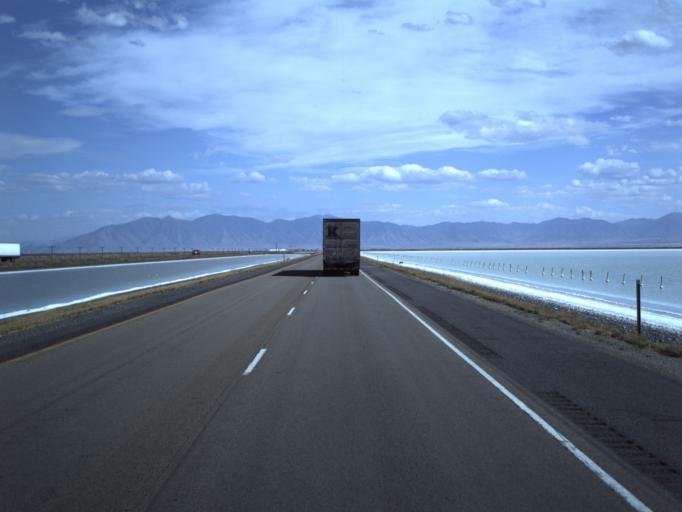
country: US
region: Utah
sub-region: Tooele County
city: Grantsville
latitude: 40.7327
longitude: -112.5987
